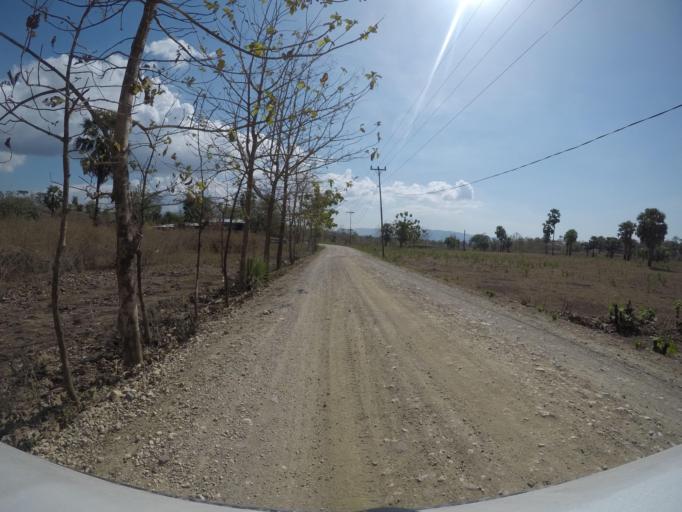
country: TL
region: Bobonaro
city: Maliana
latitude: -8.9947
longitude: 125.2023
